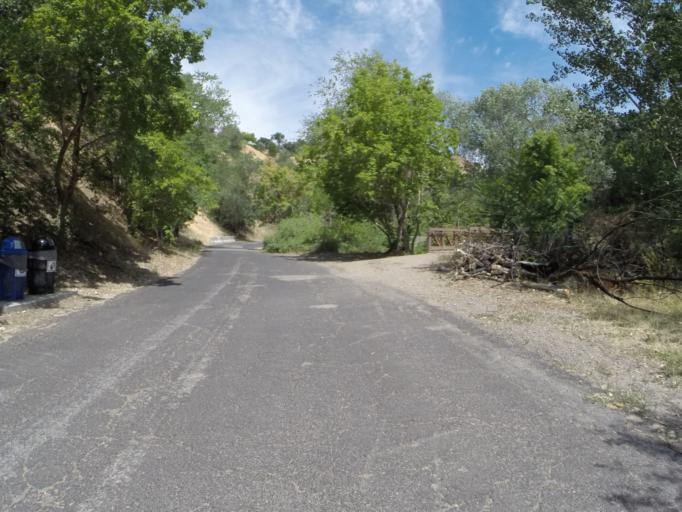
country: US
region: Utah
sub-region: Salt Lake County
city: Salt Lake City
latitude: 40.7846
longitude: -111.8834
